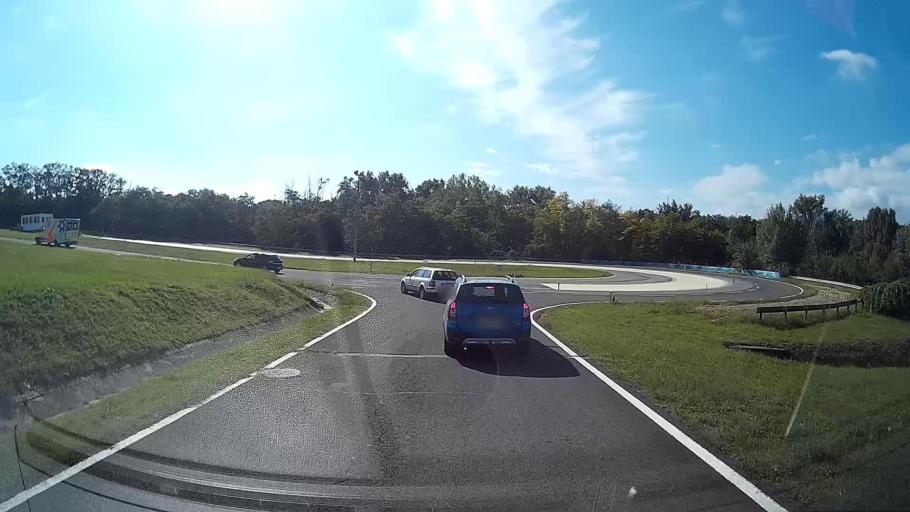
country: HU
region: Pest
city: Mogyorod
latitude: 47.5853
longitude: 19.2502
